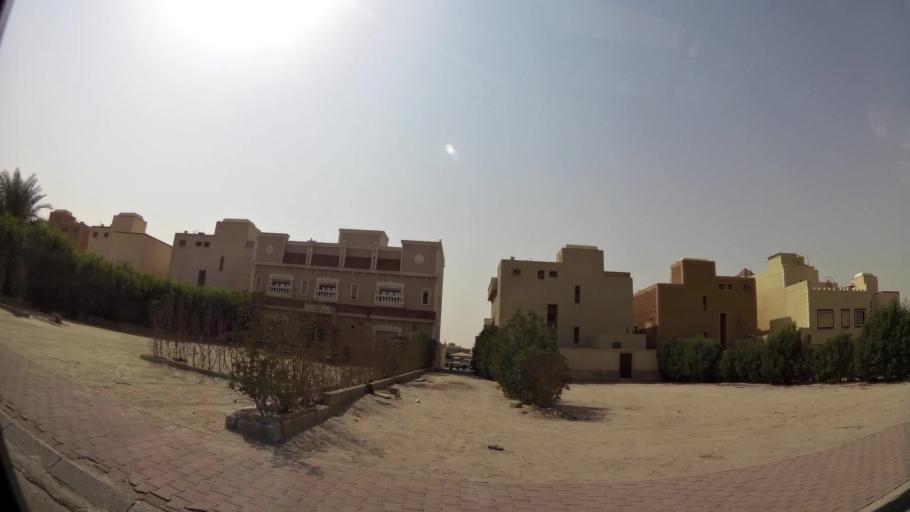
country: KW
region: Muhafazat al Jahra'
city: Al Jahra'
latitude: 29.3195
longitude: 47.7379
